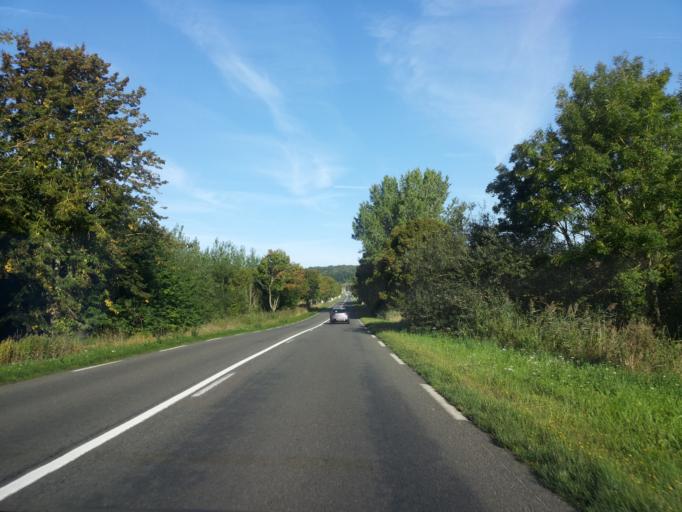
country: FR
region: Picardie
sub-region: Departement de l'Aisne
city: Crepy
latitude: 49.6013
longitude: 3.5124
